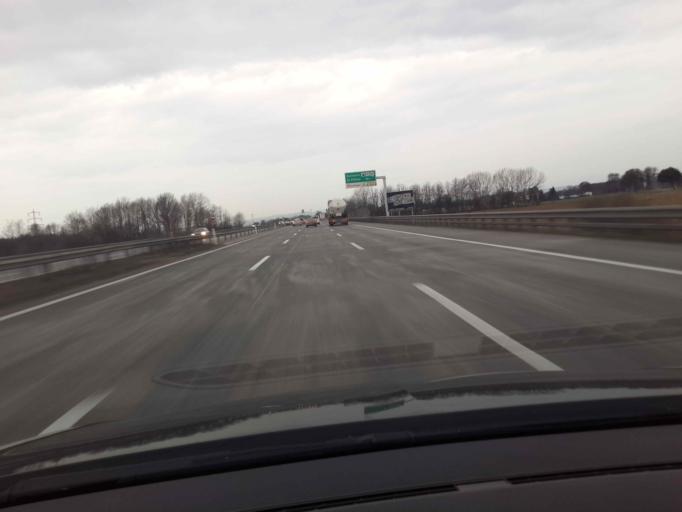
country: AT
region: Lower Austria
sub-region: Politischer Bezirk Sankt Polten
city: Gerersdorf
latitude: 48.1775
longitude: 15.5783
